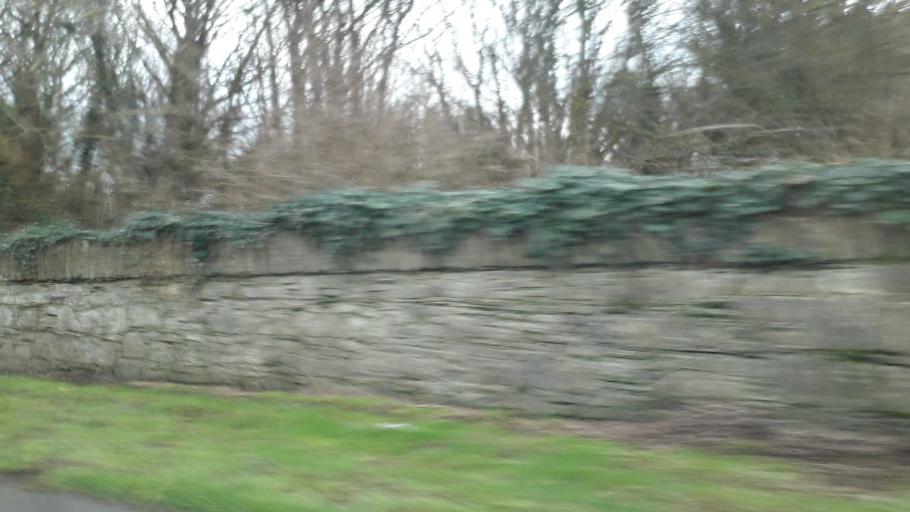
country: IE
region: Leinster
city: An Ros
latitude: 53.5383
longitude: -6.0917
